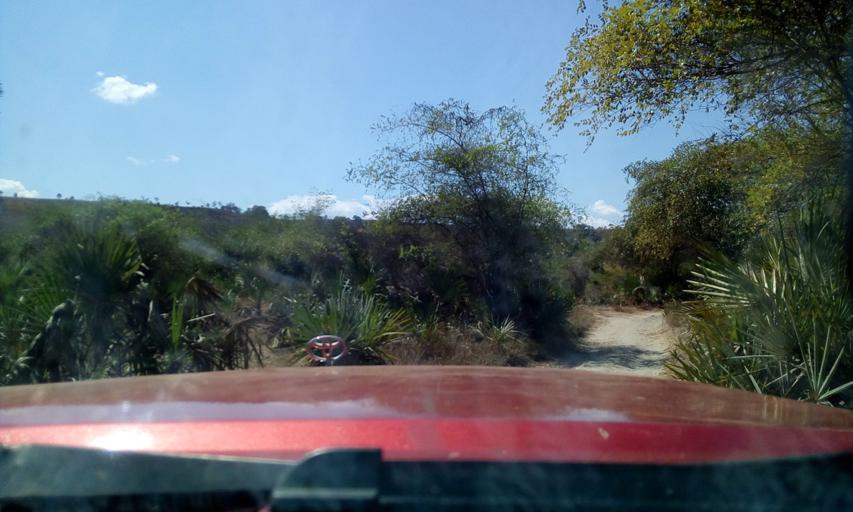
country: MG
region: Boeny
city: Sitampiky
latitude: -16.1276
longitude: 45.4900
